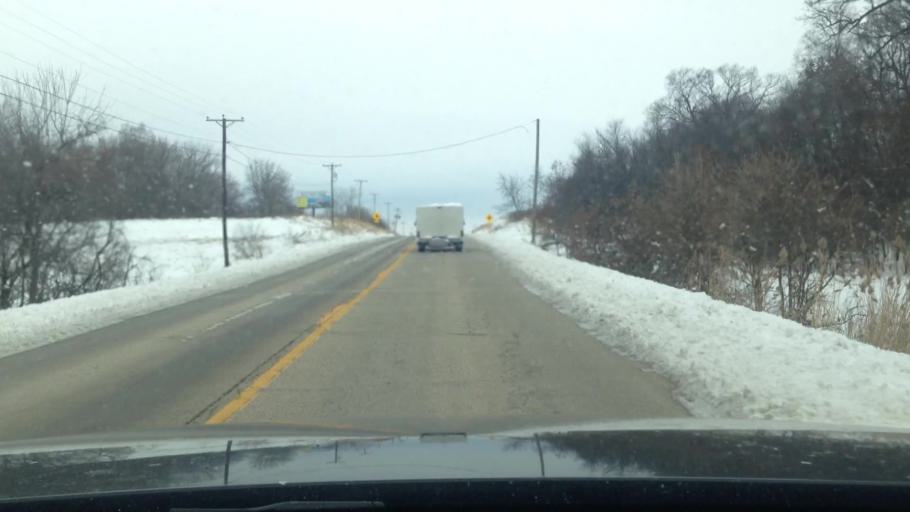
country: US
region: Illinois
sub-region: McHenry County
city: Hebron
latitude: 42.4907
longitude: -88.4424
